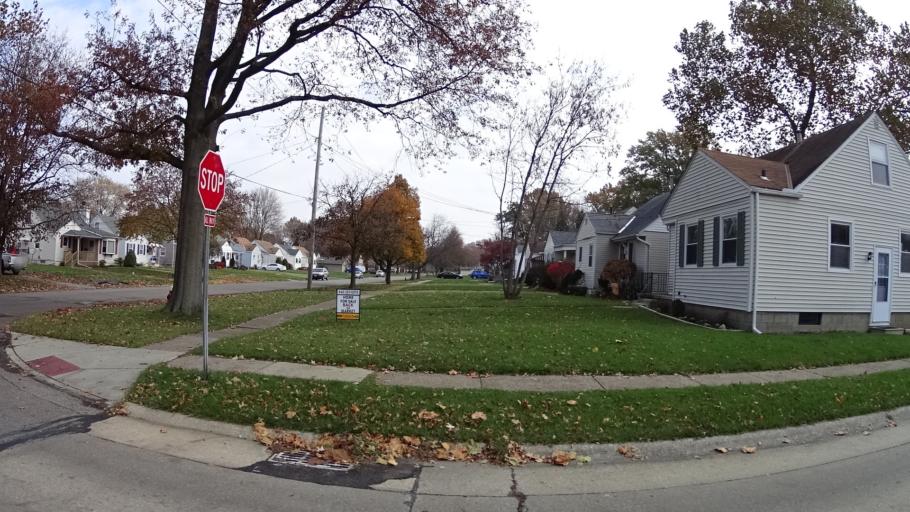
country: US
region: Ohio
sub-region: Lorain County
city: Elyria
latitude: 41.3631
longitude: -82.0861
